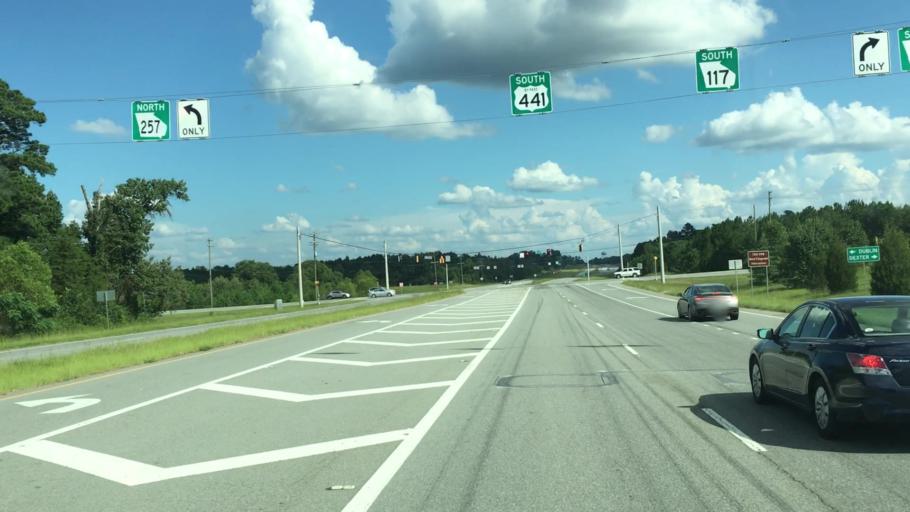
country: US
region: Georgia
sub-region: Laurens County
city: Dublin
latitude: 32.5168
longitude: -82.9575
